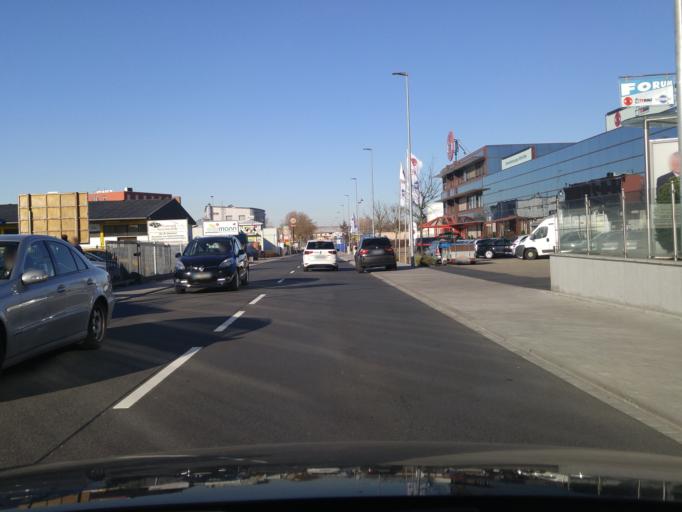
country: DE
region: Baden-Wuerttemberg
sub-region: Karlsruhe Region
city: Sinsheim
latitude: 49.2401
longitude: 8.8983
